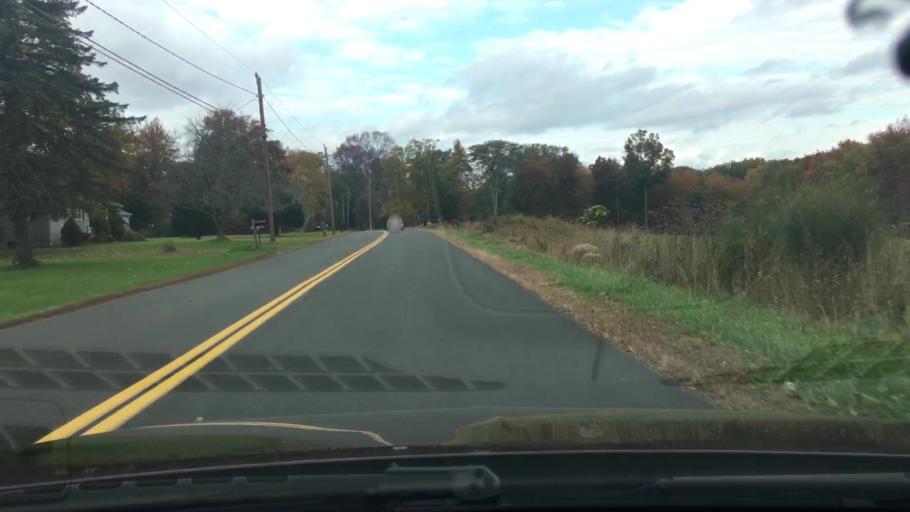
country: US
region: Connecticut
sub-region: Tolland County
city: Ellington
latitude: 41.9450
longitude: -72.4809
